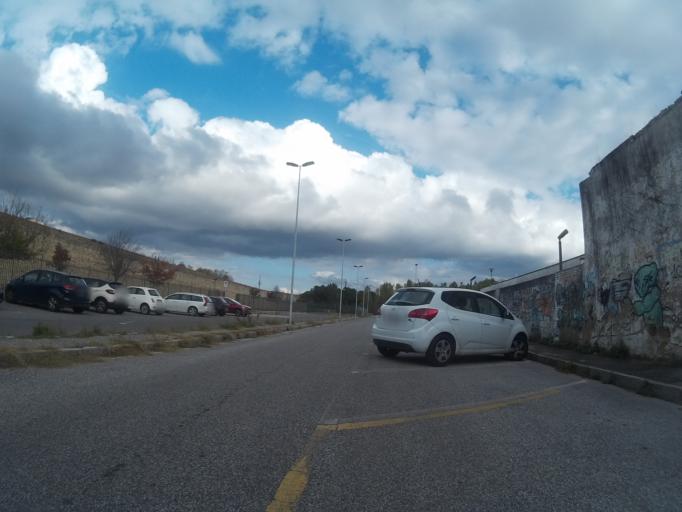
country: IT
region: Tuscany
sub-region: Provincia di Livorno
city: Livorno
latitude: 43.5599
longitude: 10.3205
